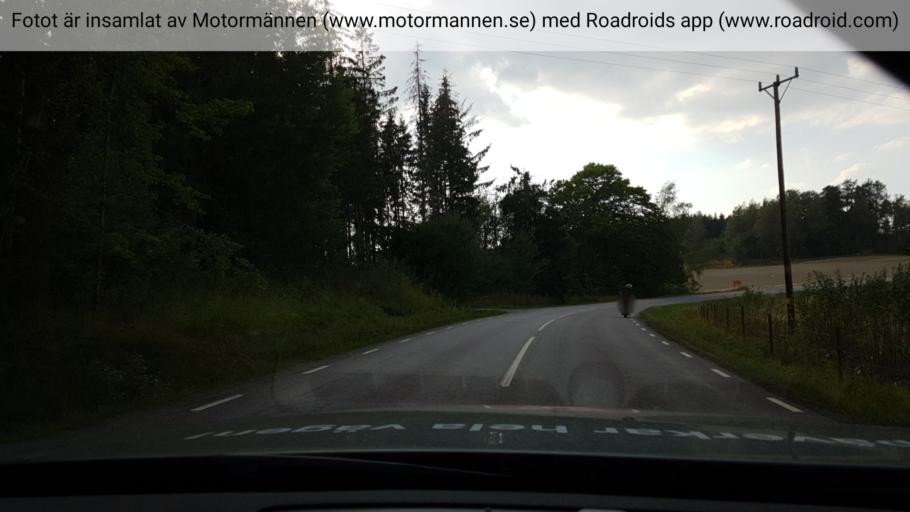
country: SE
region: Soedermanland
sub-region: Gnesta Kommun
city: Gnesta
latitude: 59.0621
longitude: 17.2981
